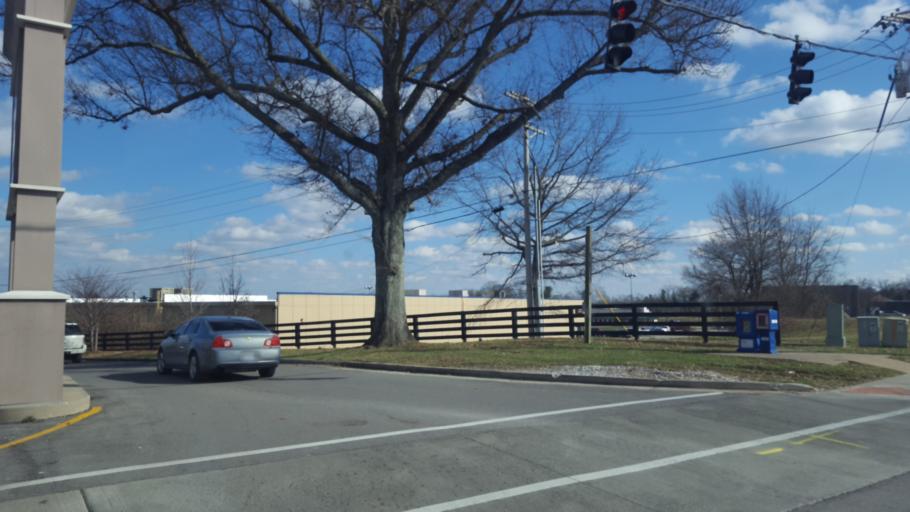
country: US
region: Kentucky
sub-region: Franklin County
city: Frankfort
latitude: 38.1975
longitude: -84.8301
